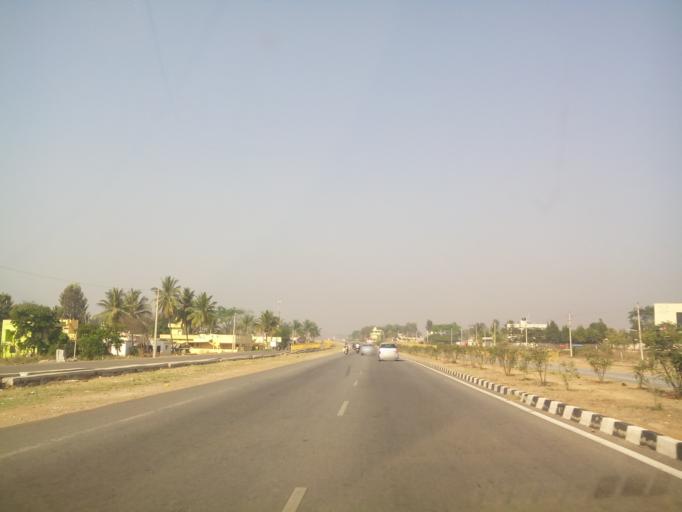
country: IN
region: Karnataka
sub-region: Bangalore Rural
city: Nelamangala
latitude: 13.0647
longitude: 77.3513
